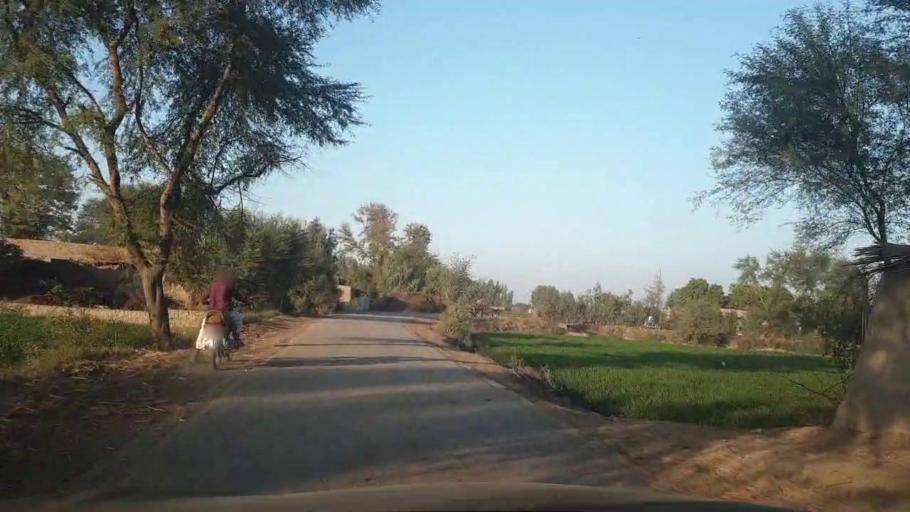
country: PK
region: Sindh
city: Ubauro
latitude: 28.1710
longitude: 69.5832
